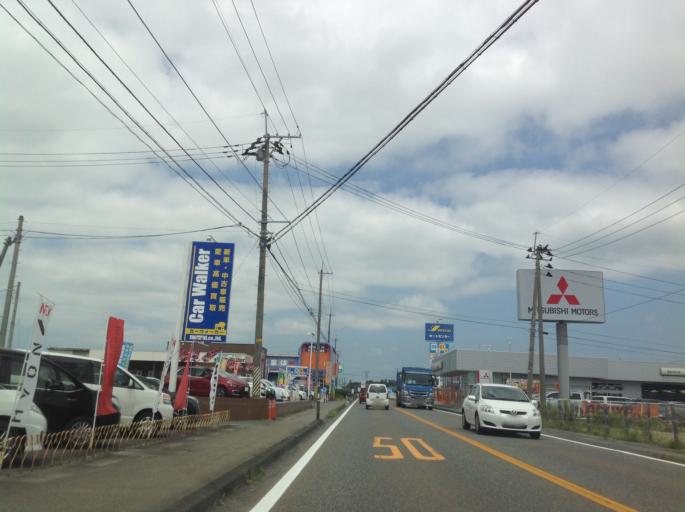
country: JP
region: Iwate
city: Mizusawa
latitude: 39.1620
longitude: 141.1441
